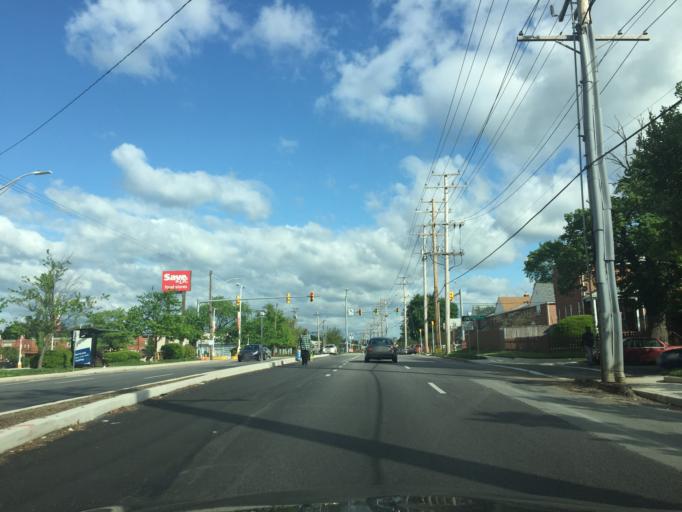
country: US
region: Maryland
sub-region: Baltimore County
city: Pikesville
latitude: 39.3601
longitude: -76.7074
